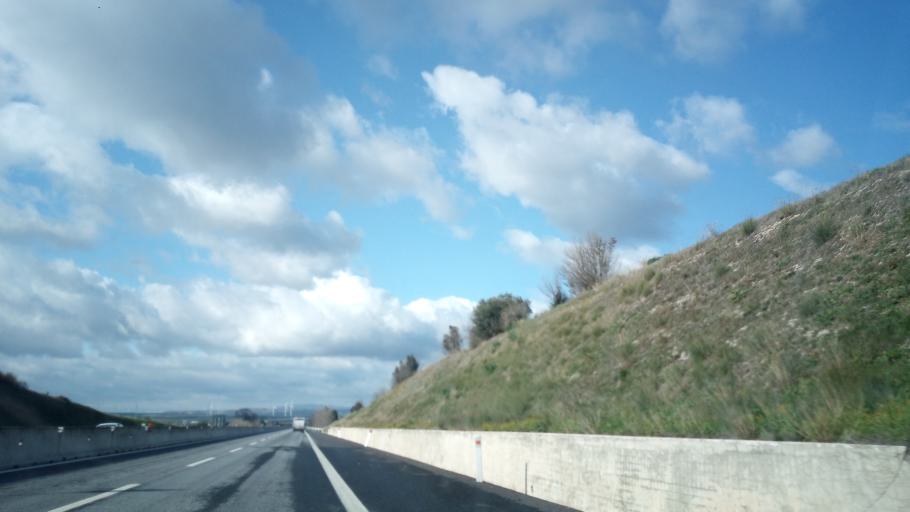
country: IT
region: Apulia
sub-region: Provincia di Foggia
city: Stornarella
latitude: 41.1793
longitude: 15.7168
